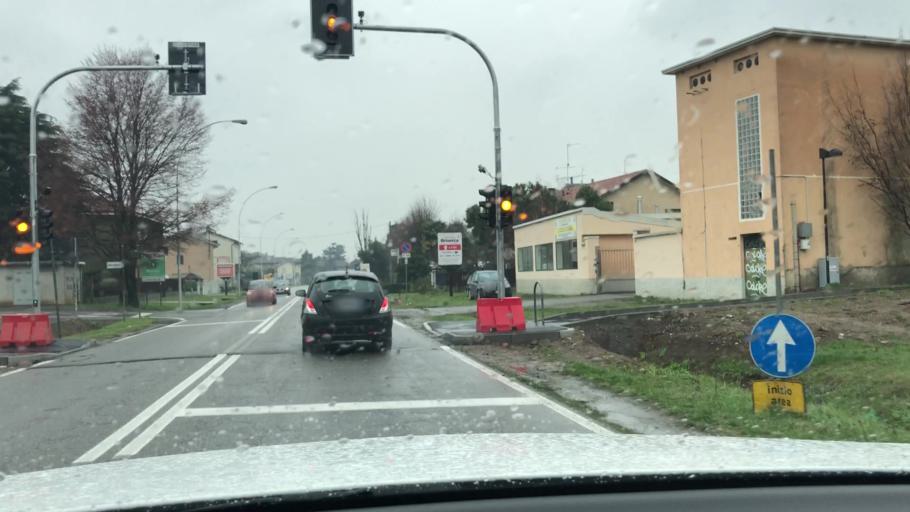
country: IT
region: Lombardy
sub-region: Provincia di Monza e Brianza
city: Muggio
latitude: 45.5899
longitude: 9.2129
